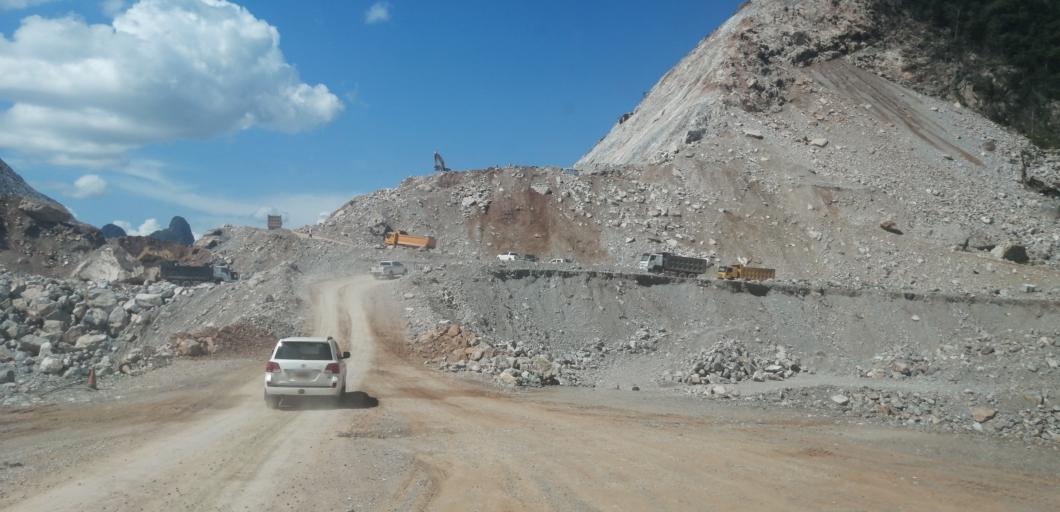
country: LA
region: Vientiane
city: Vangviang
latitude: 18.8688
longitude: 102.4273
